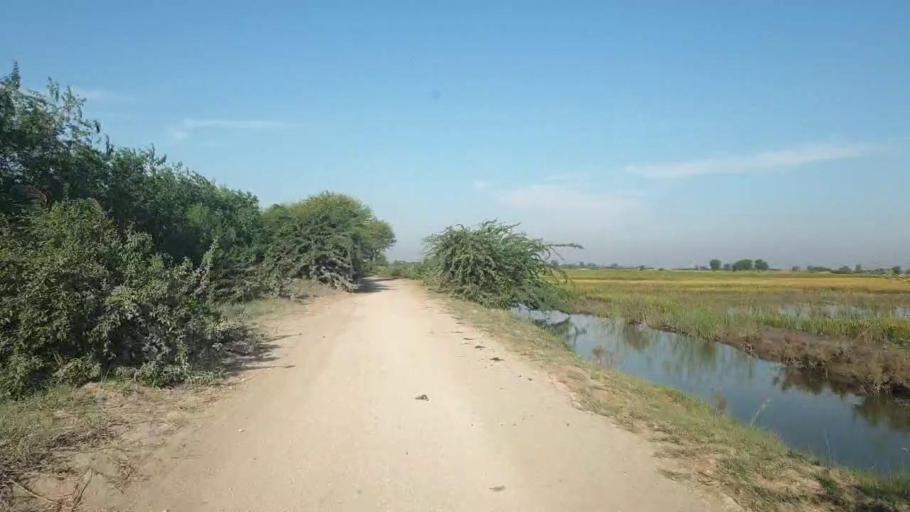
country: PK
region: Sindh
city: Talhar
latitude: 24.8231
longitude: 68.8322
